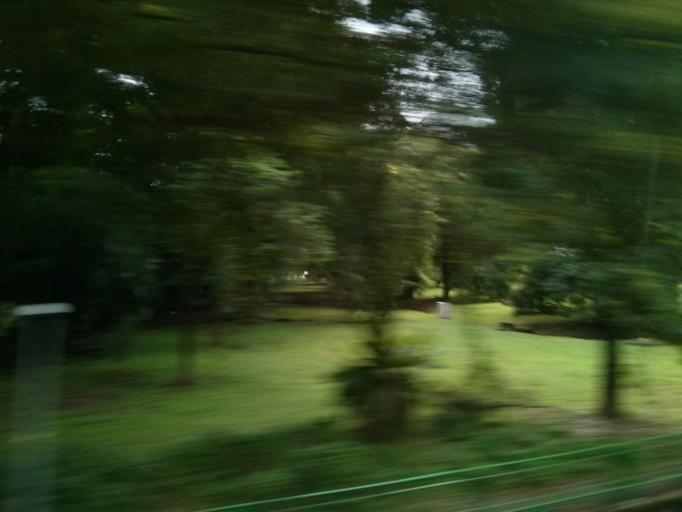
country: SG
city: Singapore
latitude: 1.2974
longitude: 103.7834
